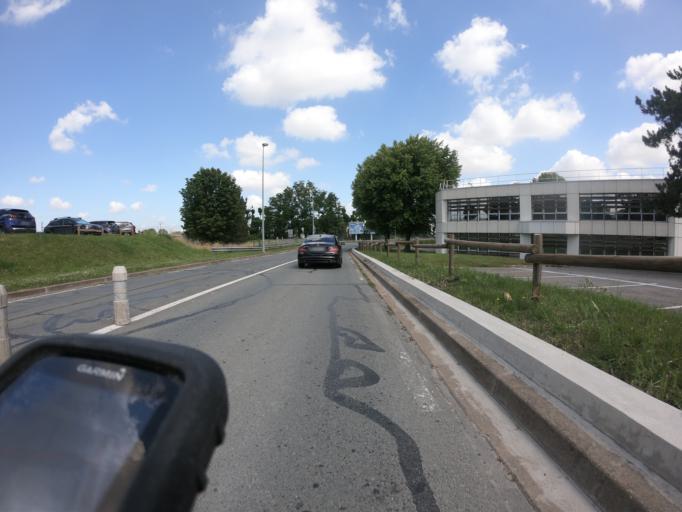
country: FR
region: Ile-de-France
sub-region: Departement du Val-de-Marne
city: Rungis
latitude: 48.7419
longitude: 2.3596
